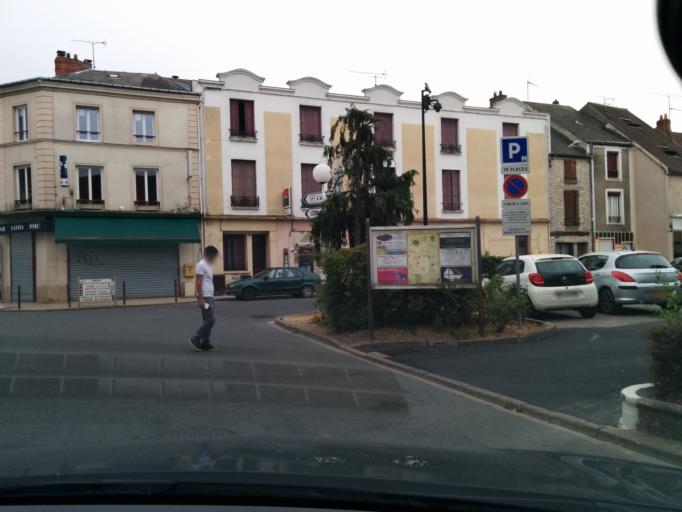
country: FR
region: Ile-de-France
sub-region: Departement de l'Essonne
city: Angerville
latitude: 48.3124
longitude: 1.9988
